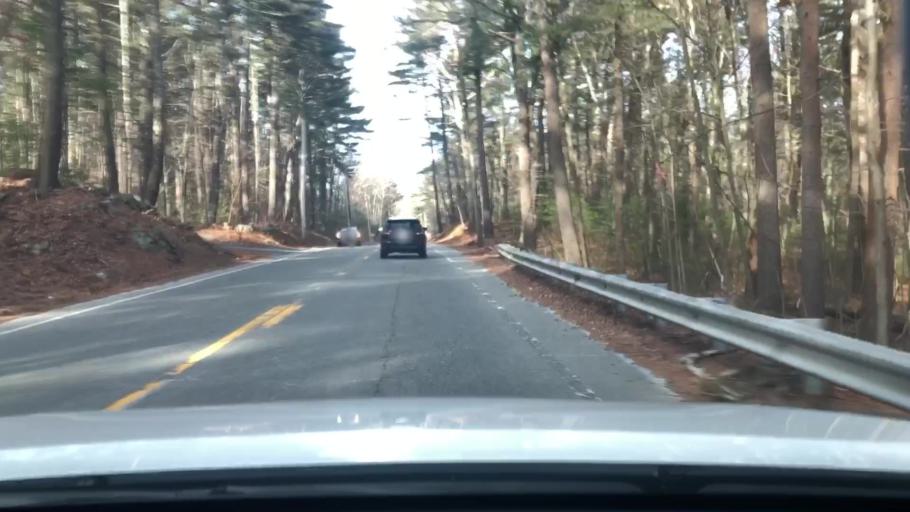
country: US
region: Massachusetts
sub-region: Worcester County
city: Grafton
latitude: 42.1962
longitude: -71.6563
